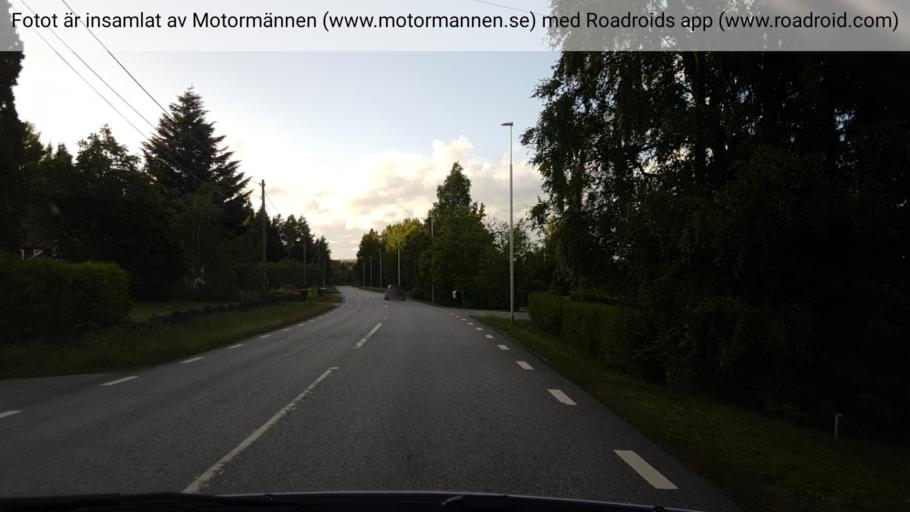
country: SE
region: OErebro
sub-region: Karlskoga Kommun
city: Karlskoga
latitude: 59.3678
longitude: 14.5730
